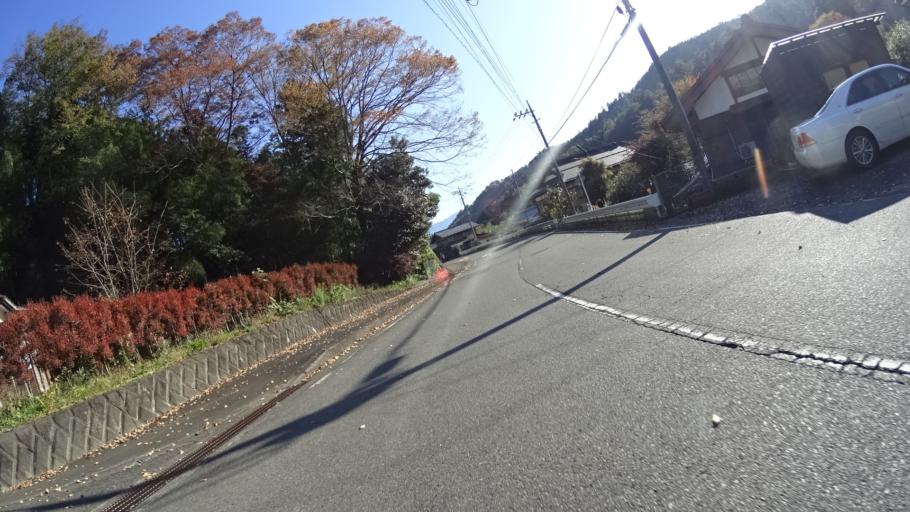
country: JP
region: Yamanashi
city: Uenohara
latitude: 35.6494
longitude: 139.1221
